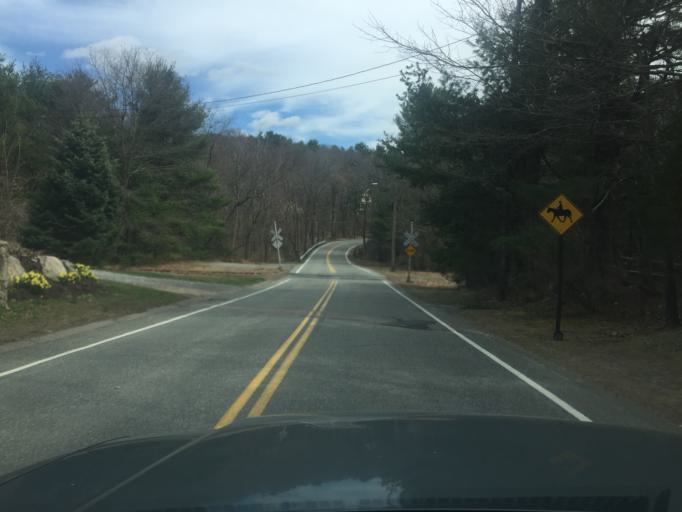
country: US
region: Massachusetts
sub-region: Norfolk County
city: Medfield
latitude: 42.2112
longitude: -71.3146
